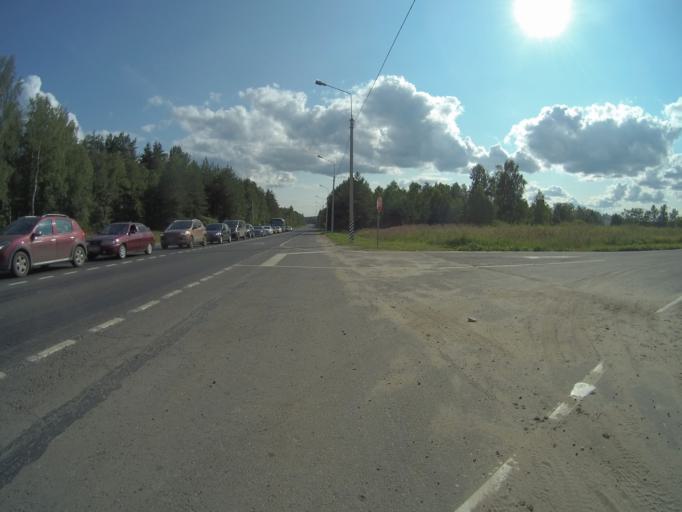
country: RU
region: Ivanovo
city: Novoye Leushino
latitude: 56.6905
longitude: 40.6186
